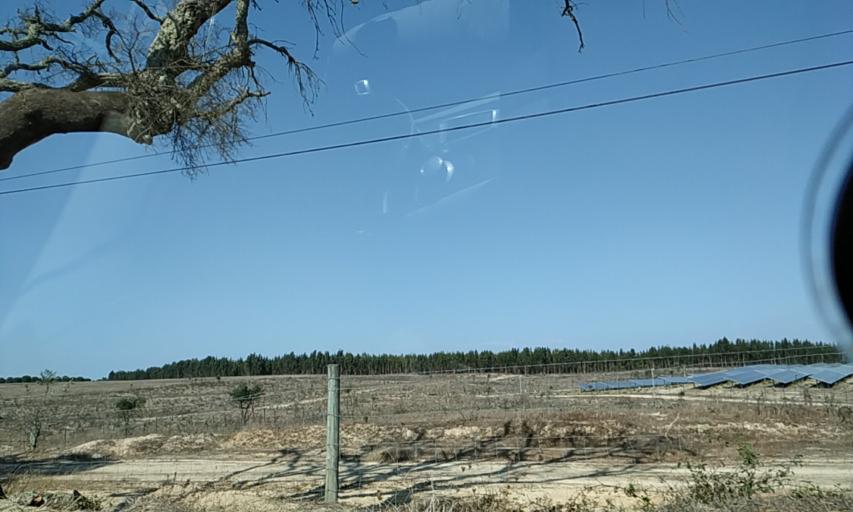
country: PT
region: Evora
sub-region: Vendas Novas
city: Vendas Novas
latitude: 38.7305
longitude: -8.6232
